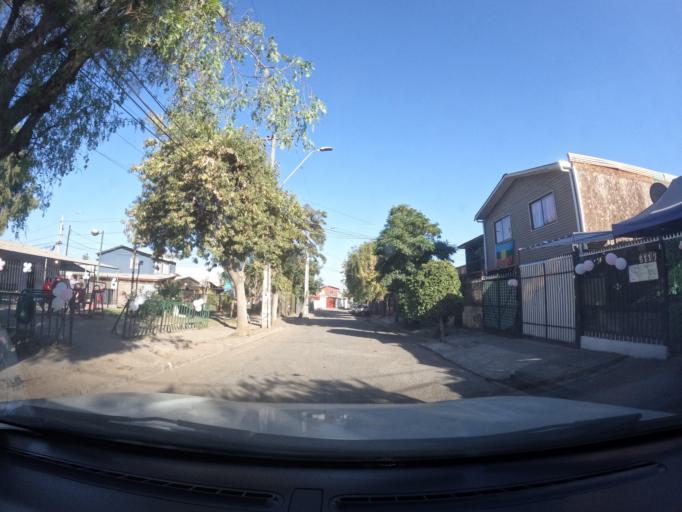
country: CL
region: Santiago Metropolitan
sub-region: Provincia de Santiago
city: Villa Presidente Frei, Nunoa, Santiago, Chile
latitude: -33.5022
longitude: -70.5671
